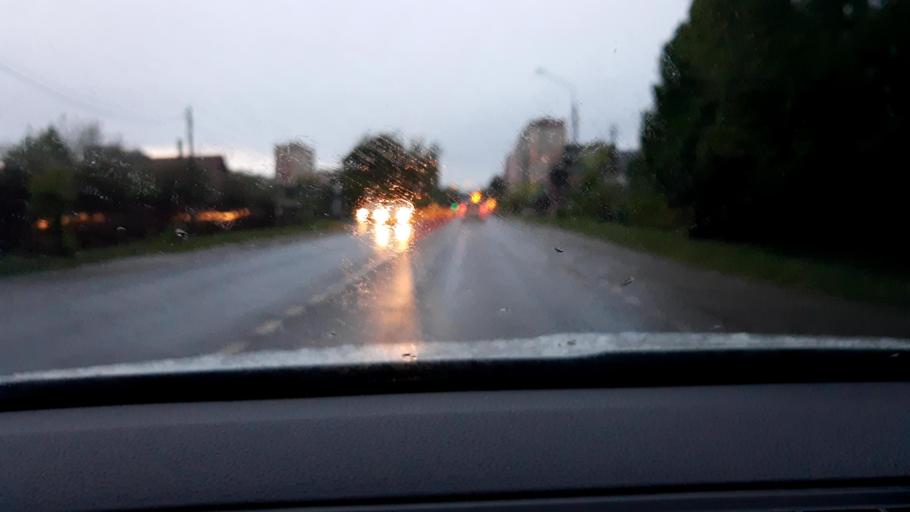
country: RU
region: Moskovskaya
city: Shchelkovo
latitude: 55.9322
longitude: 37.9804
